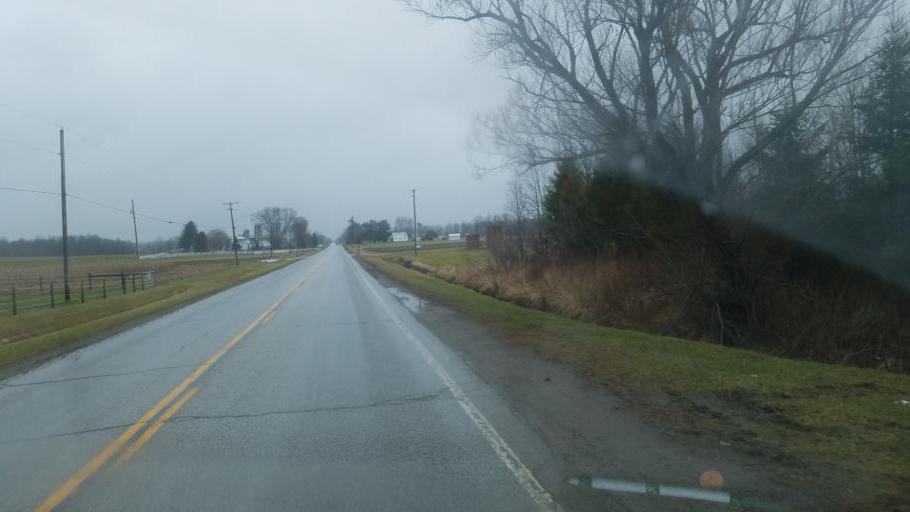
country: US
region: Ohio
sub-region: Geauga County
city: Middlefield
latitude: 41.4286
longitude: -80.9556
